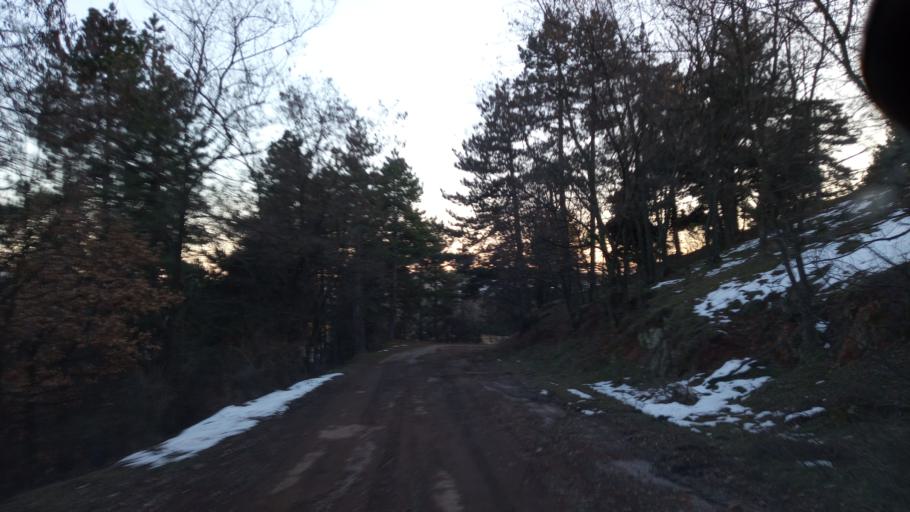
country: BG
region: Sofia-Capital
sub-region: Stolichna Obshtina
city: Bukhovo
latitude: 42.7932
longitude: 23.5281
